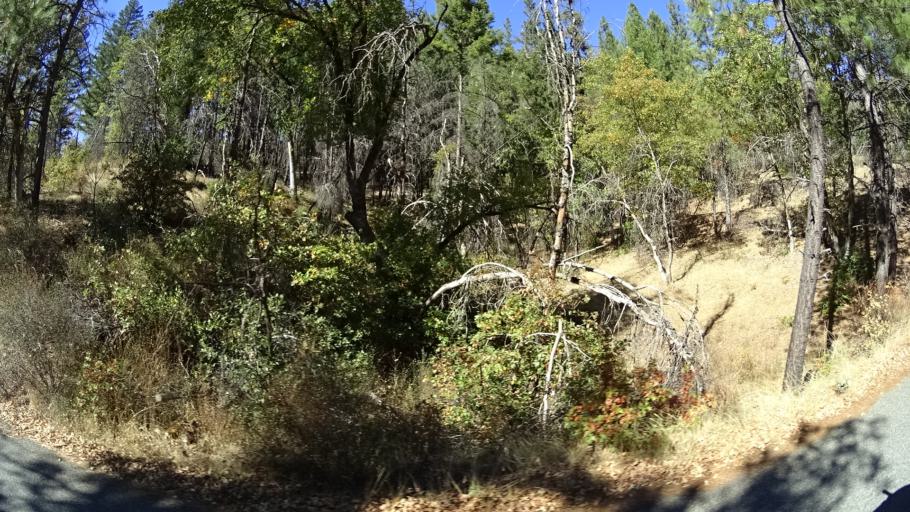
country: US
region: California
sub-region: Siskiyou County
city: Happy Camp
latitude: 41.2991
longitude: -123.2191
